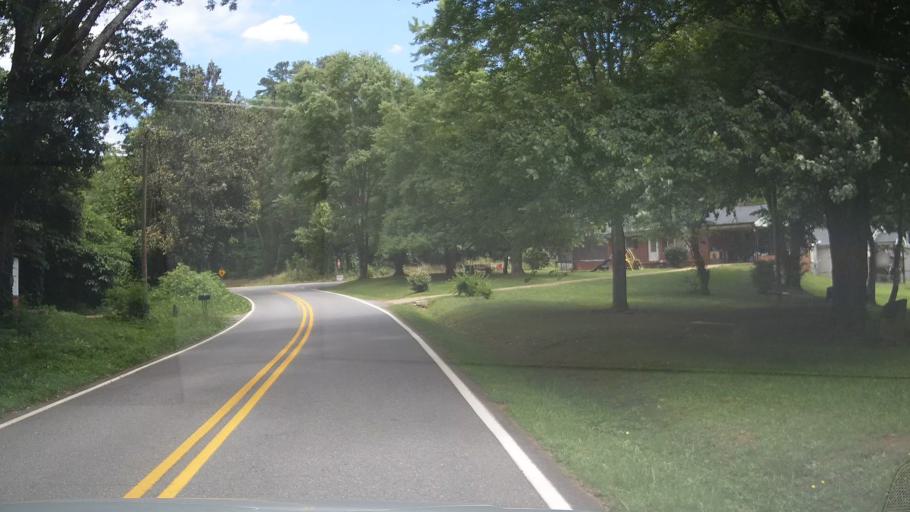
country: US
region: North Carolina
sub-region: Rutherford County
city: Rutherfordton
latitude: 35.3756
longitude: -81.9638
